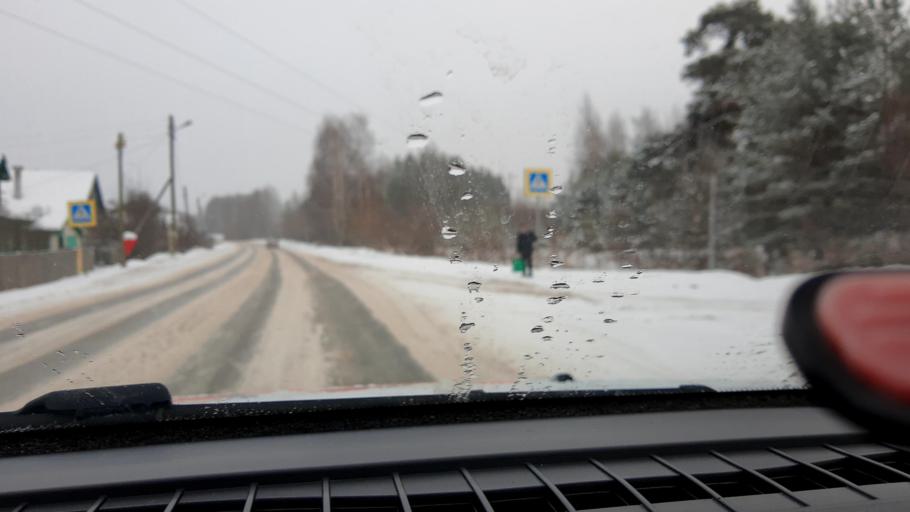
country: RU
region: Nizjnij Novgorod
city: Afonino
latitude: 56.3202
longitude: 44.1539
